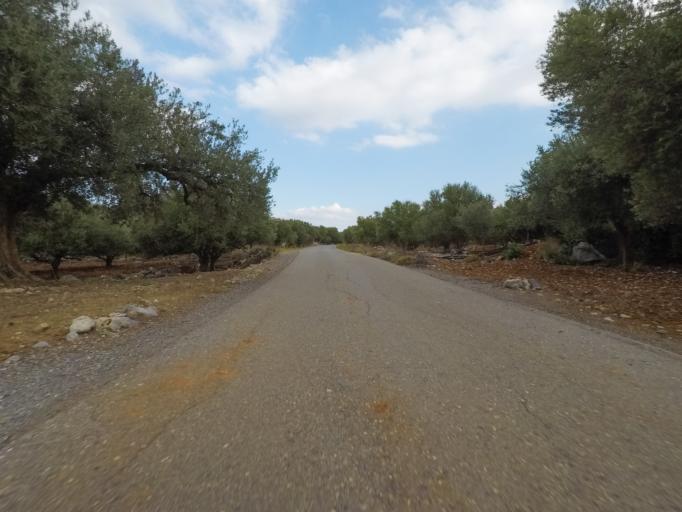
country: GR
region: Crete
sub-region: Nomos Lasithiou
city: Kritsa
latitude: 35.1746
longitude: 25.6528
